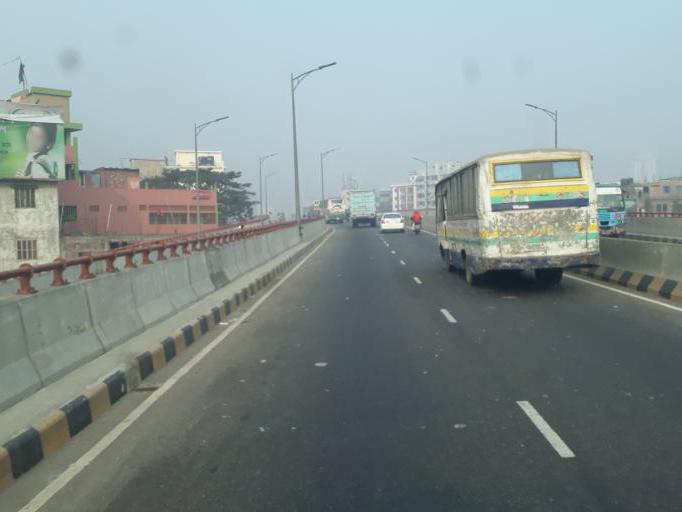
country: BD
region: Dhaka
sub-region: Dhaka
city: Dhaka
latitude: 23.7138
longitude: 90.4264
